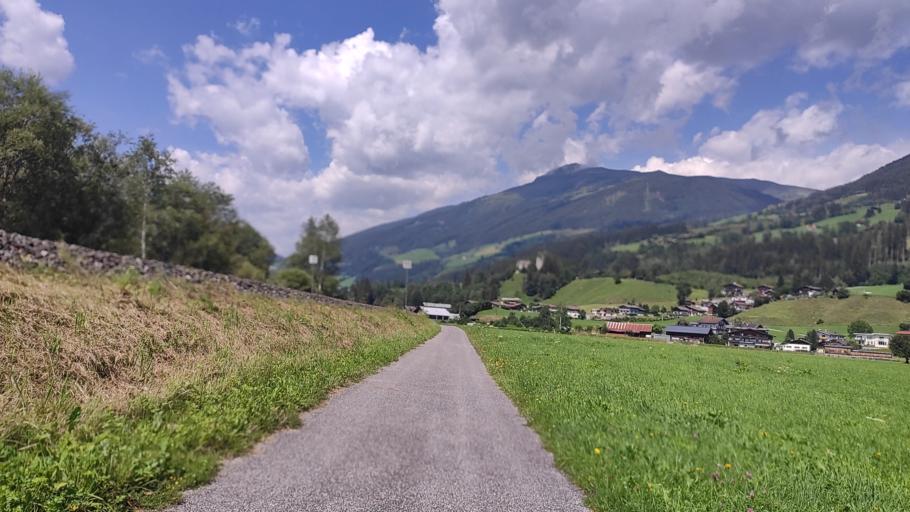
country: AT
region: Salzburg
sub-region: Politischer Bezirk Zell am See
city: Wald im Pinzgau
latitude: 47.2442
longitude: 12.2543
